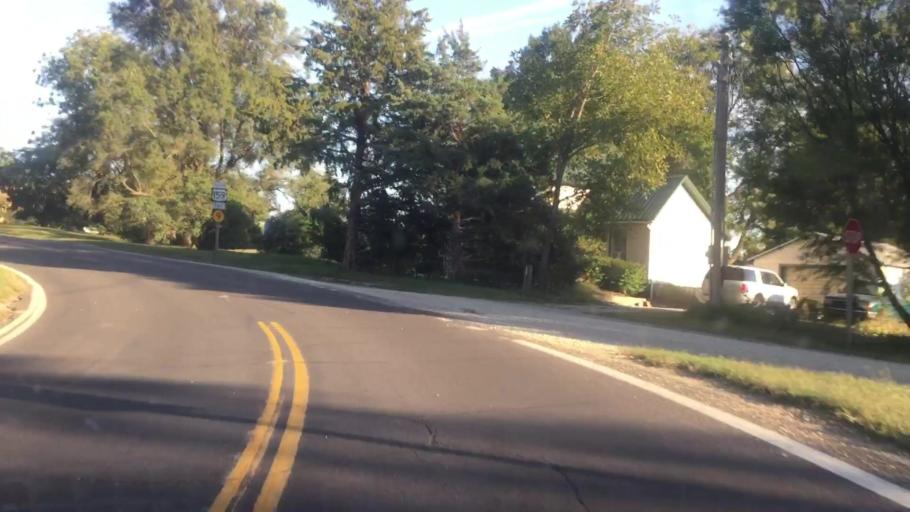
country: US
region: Kansas
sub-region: Brown County
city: Horton
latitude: 39.5505
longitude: -95.5243
